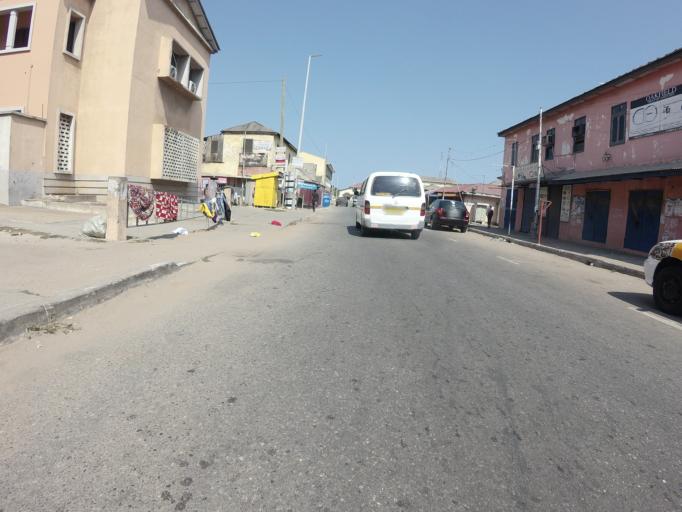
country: GH
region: Greater Accra
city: Accra
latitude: 5.5410
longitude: -0.2084
